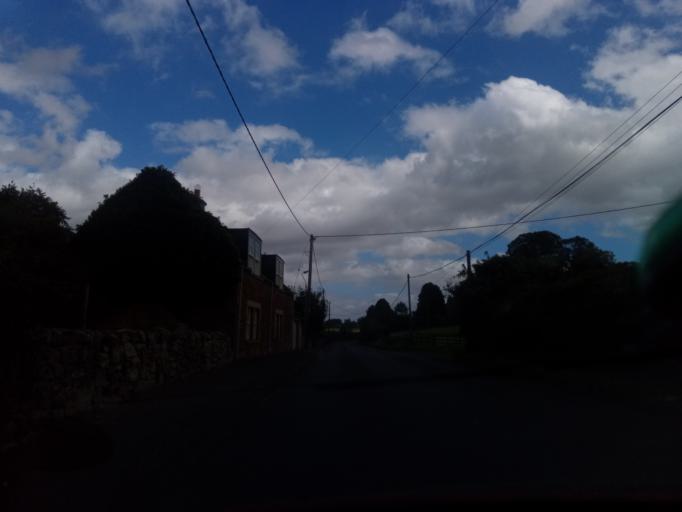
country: GB
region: Scotland
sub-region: The Scottish Borders
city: Kelso
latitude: 55.6111
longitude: -2.3882
